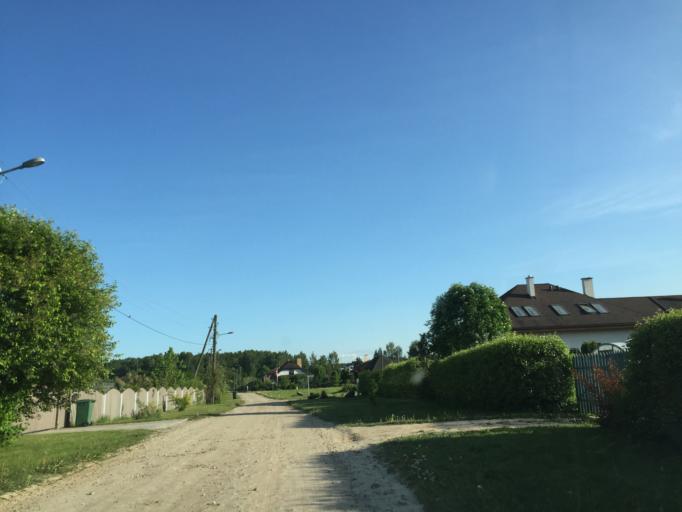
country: LV
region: Kekava
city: Kekava
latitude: 56.8248
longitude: 24.2580
